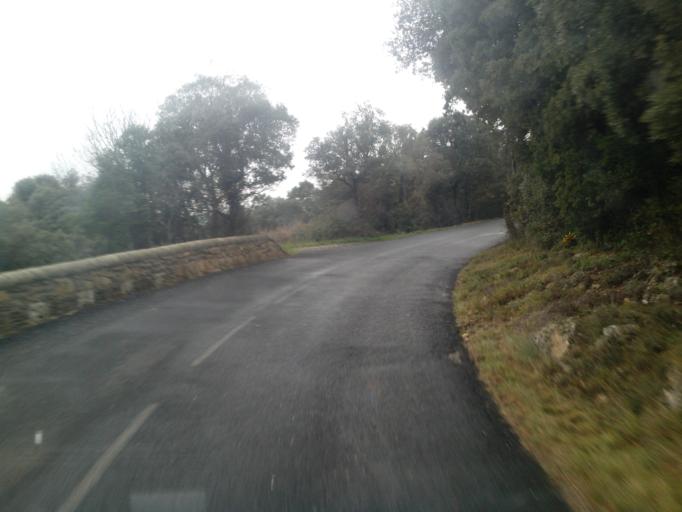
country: FR
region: Languedoc-Roussillon
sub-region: Departement de l'Herault
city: Saint-Martin-de-Londres
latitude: 43.8232
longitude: 3.6774
